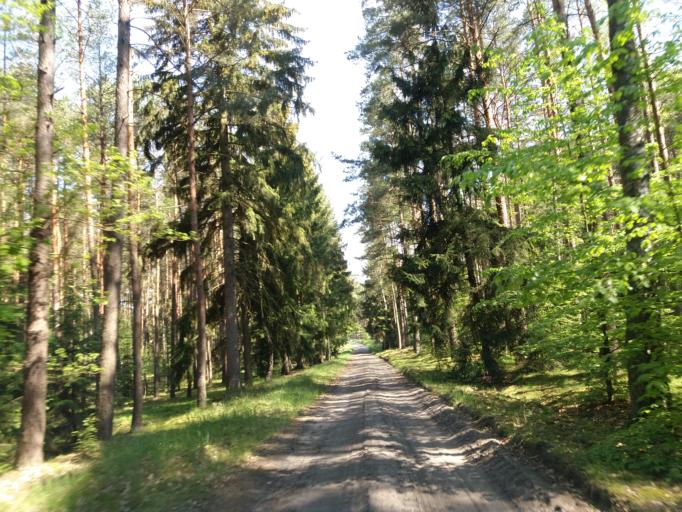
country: PL
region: West Pomeranian Voivodeship
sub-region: Powiat choszczenski
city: Bierzwnik
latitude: 53.0921
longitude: 15.7149
